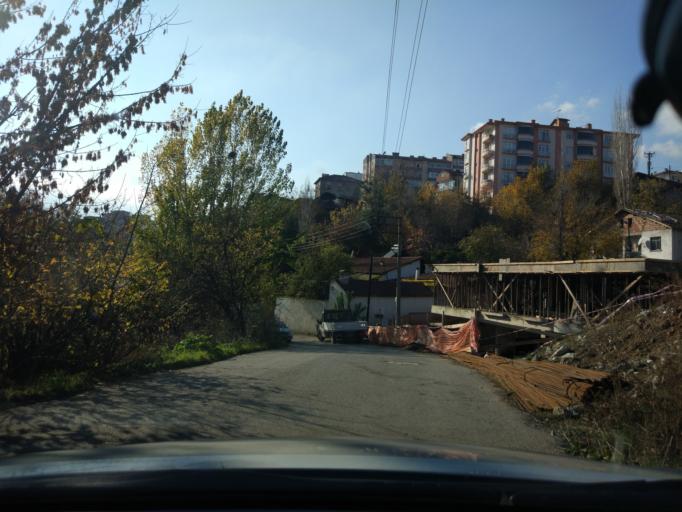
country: TR
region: Karabuk
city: Karabuk
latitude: 41.2049
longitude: 32.6306
